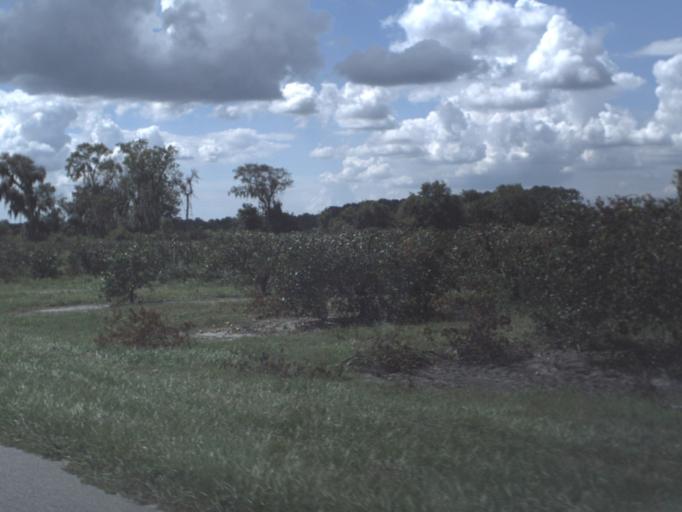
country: US
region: Florida
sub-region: Hillsborough County
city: Wimauma
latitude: 27.5814
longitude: -82.1869
